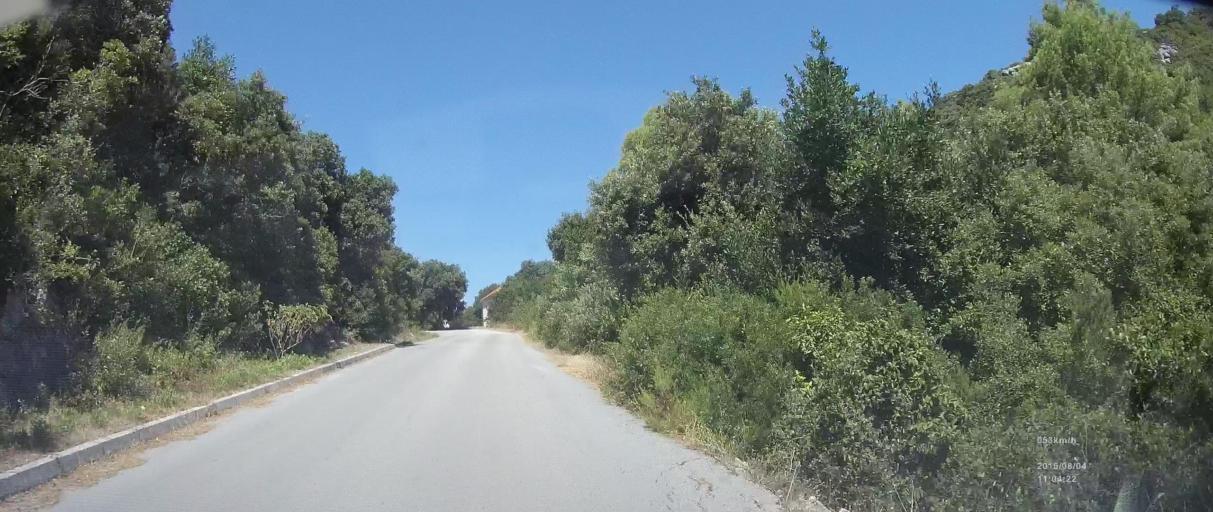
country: HR
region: Dubrovacko-Neretvanska
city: Blato
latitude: 42.7776
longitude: 17.4542
